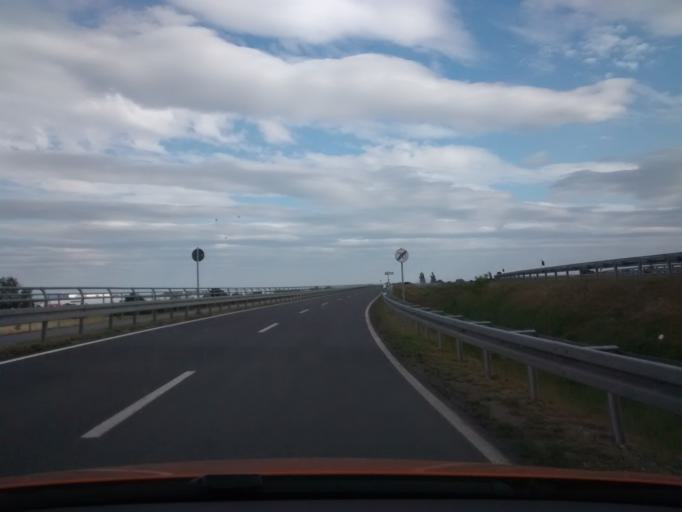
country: DE
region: Berlin
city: Bohnsdorf
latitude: 52.3767
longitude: 13.5488
